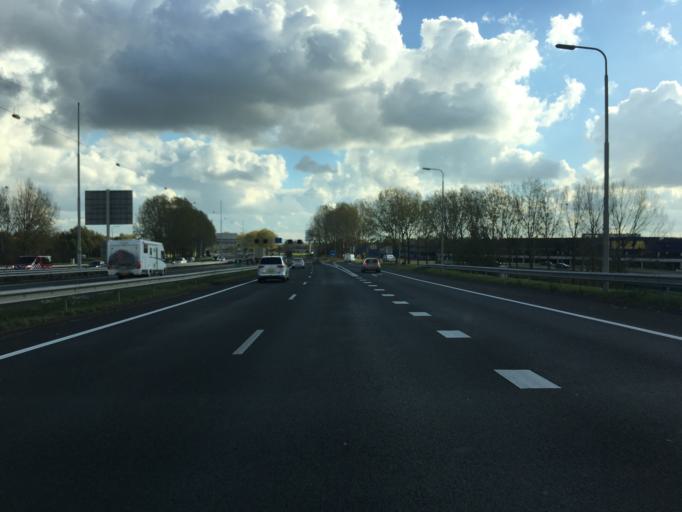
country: NL
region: Gelderland
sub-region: Gemeente Westervoort
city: Westervoort
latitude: 51.9705
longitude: 5.9945
